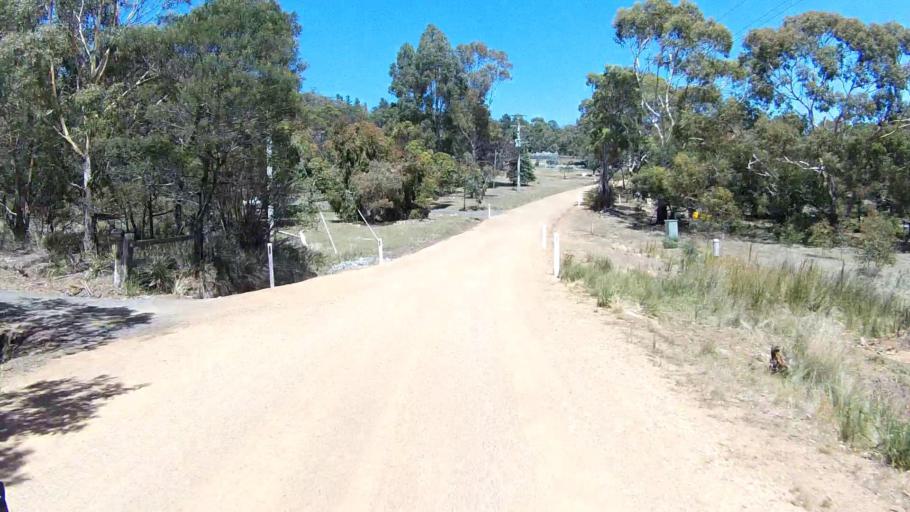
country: AU
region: Tasmania
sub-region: Clarence
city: Cambridge
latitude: -42.8511
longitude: 147.4377
